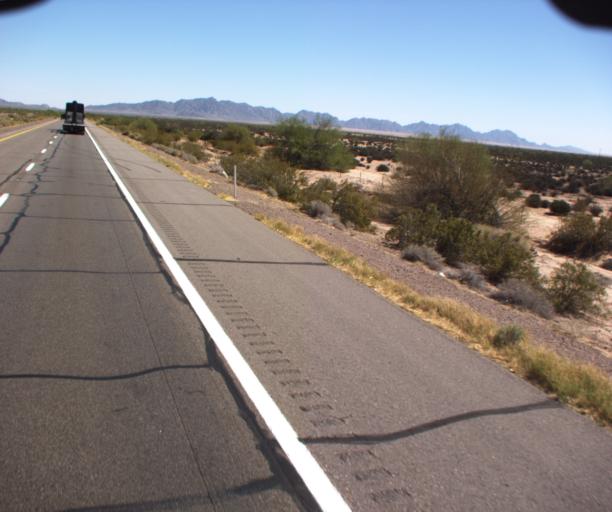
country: US
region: Arizona
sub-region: Yuma County
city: Wellton
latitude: 32.7026
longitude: -113.8927
